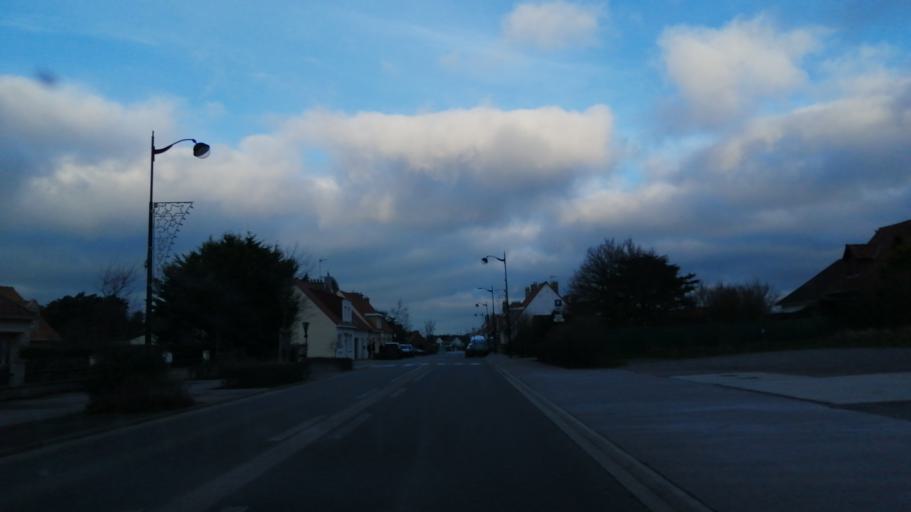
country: FR
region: Nord-Pas-de-Calais
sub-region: Departement du Pas-de-Calais
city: Ambleteuse
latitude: 50.8504
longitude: 1.6103
